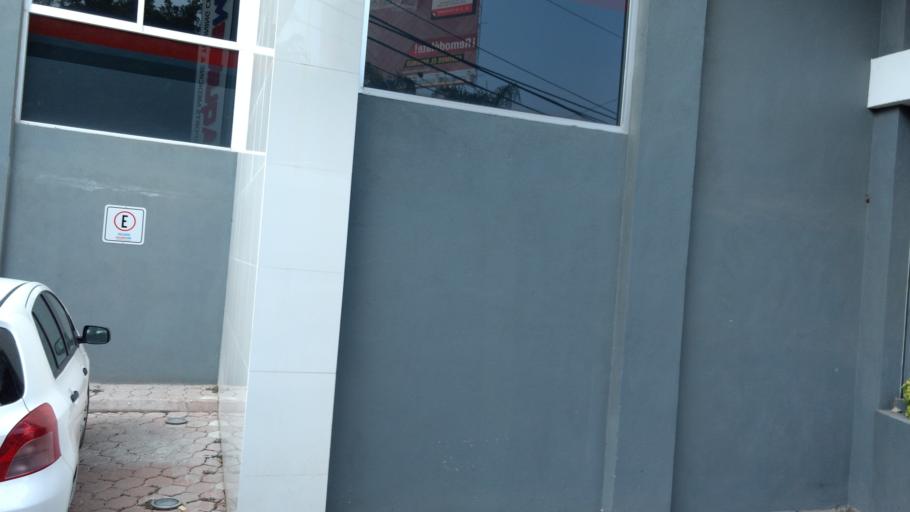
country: MX
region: Guanajuato
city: Leon
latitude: 21.1481
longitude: -101.6880
